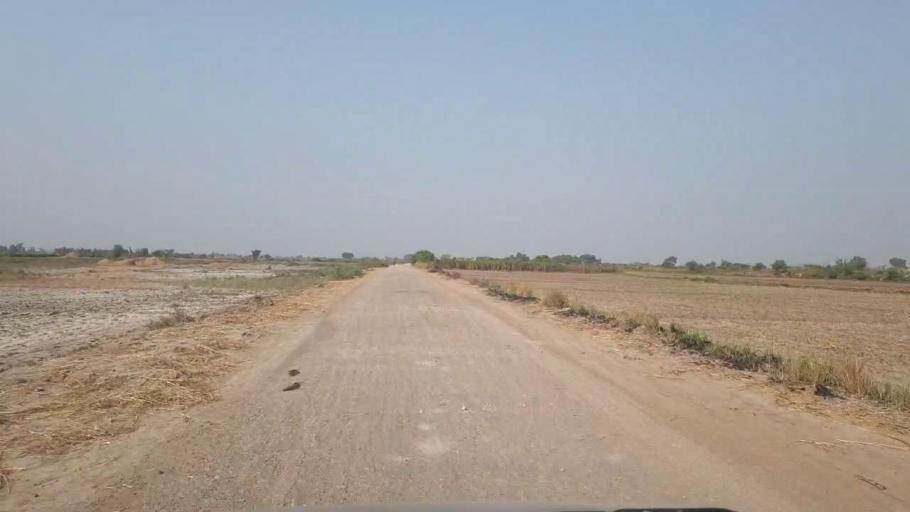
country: PK
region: Sindh
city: Tando Muhammad Khan
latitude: 25.0879
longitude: 68.3393
